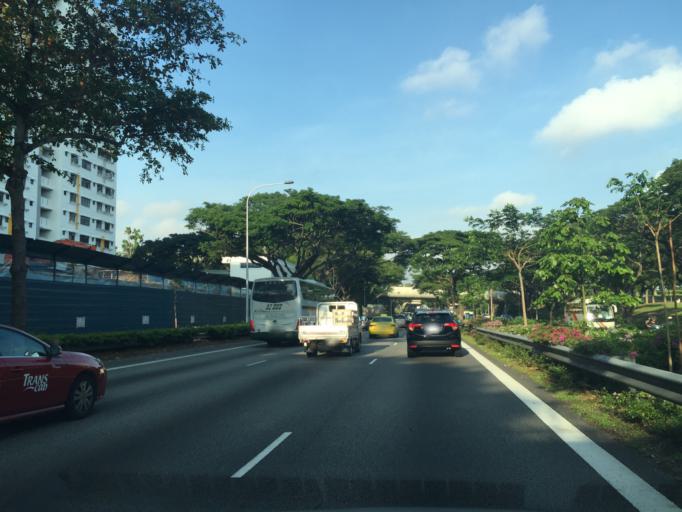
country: SG
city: Singapore
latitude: 1.3338
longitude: 103.9226
